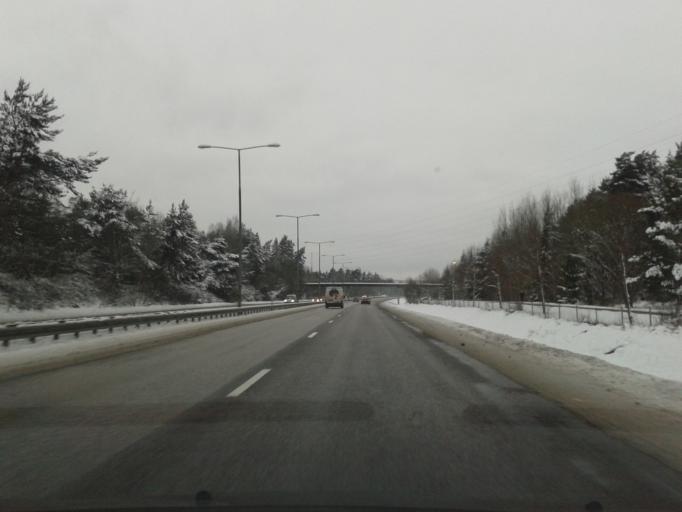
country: SE
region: Stockholm
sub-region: Stockholms Kommun
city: Arsta
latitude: 59.2588
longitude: 18.0761
